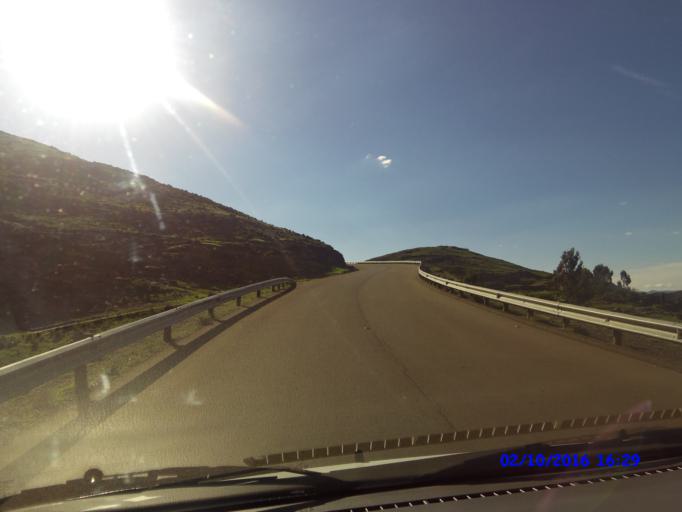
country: LS
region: Maseru
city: Nako
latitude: -29.4750
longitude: 28.0856
